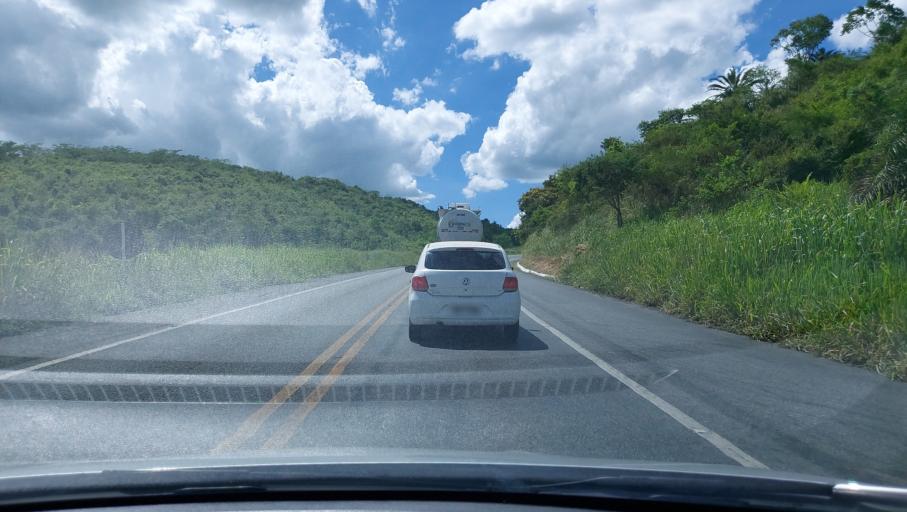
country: BR
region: Bahia
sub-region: Ruy Barbosa
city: Terra Nova
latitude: -12.4578
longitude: -40.5867
